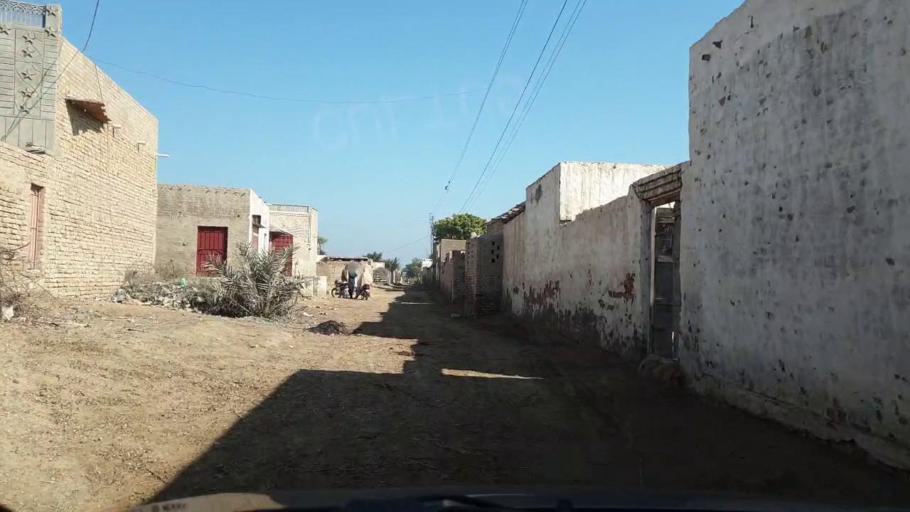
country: PK
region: Sindh
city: Sinjhoro
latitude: 25.9617
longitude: 68.7500
